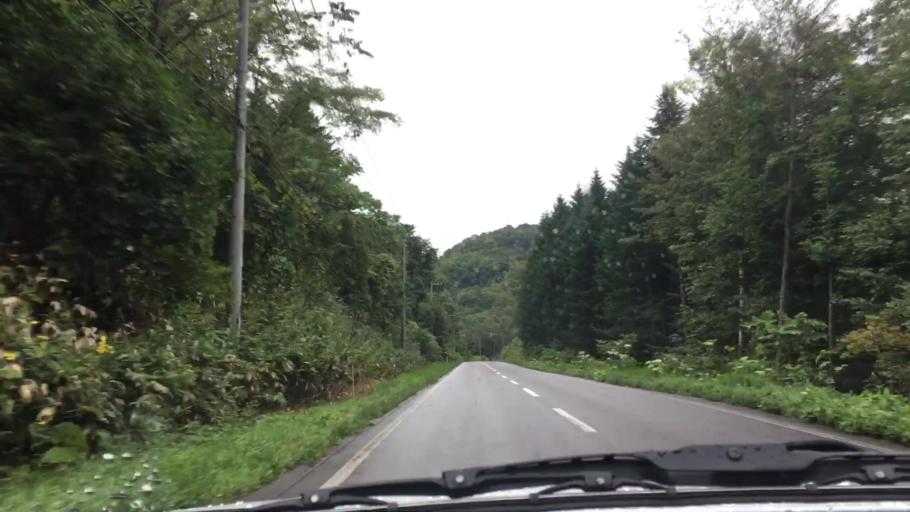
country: JP
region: Hokkaido
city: Niseko Town
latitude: 42.6169
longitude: 140.7275
